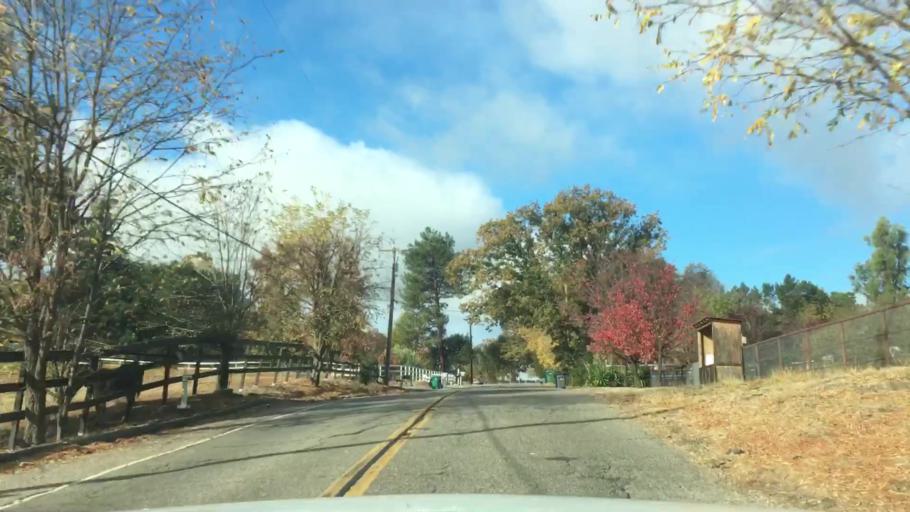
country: US
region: California
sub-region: San Luis Obispo County
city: Atascadero
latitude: 35.4582
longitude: -120.6620
